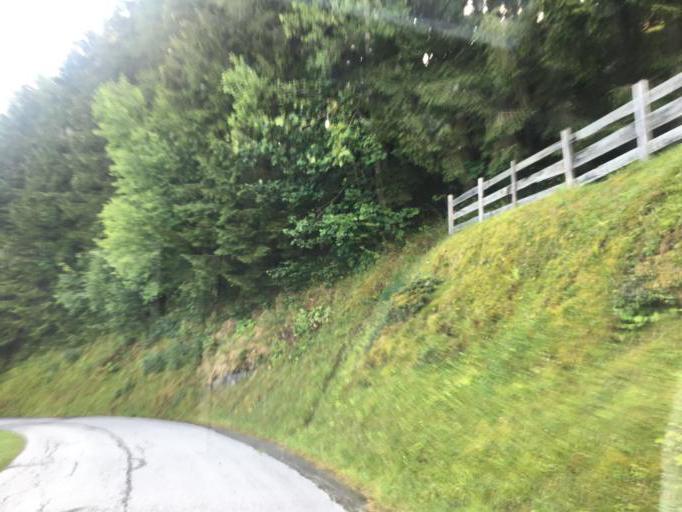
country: AT
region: Styria
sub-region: Politischer Bezirk Liezen
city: Schladming
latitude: 47.3836
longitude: 13.6588
